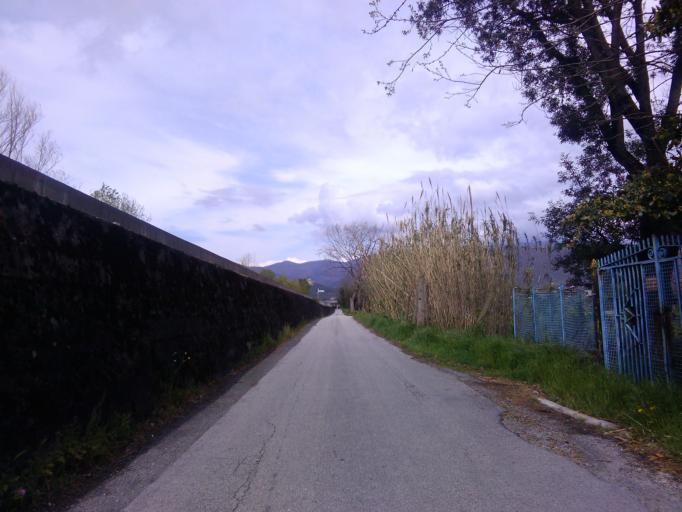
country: IT
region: Tuscany
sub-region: Provincia di Massa-Carrara
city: Marina di Carrara
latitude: 44.0510
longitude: 10.0231
